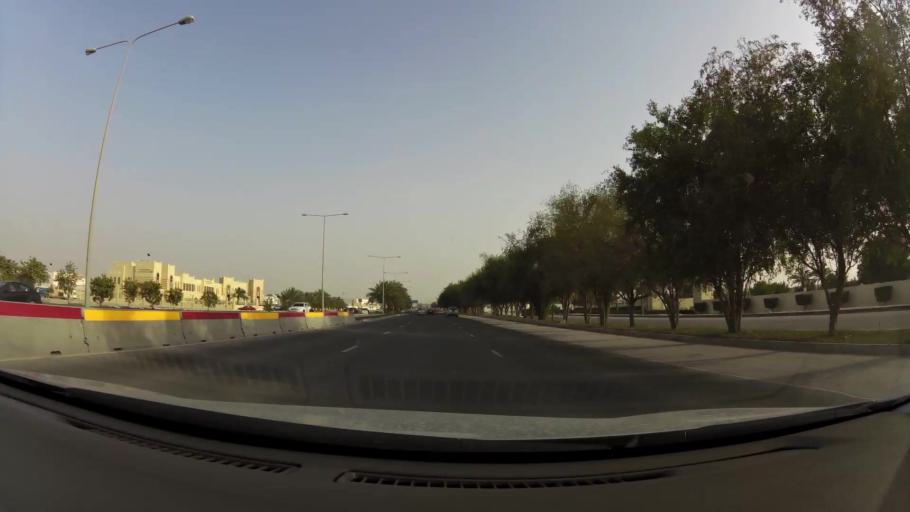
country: QA
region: Baladiyat ar Rayyan
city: Ar Rayyan
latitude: 25.2498
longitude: 51.4594
